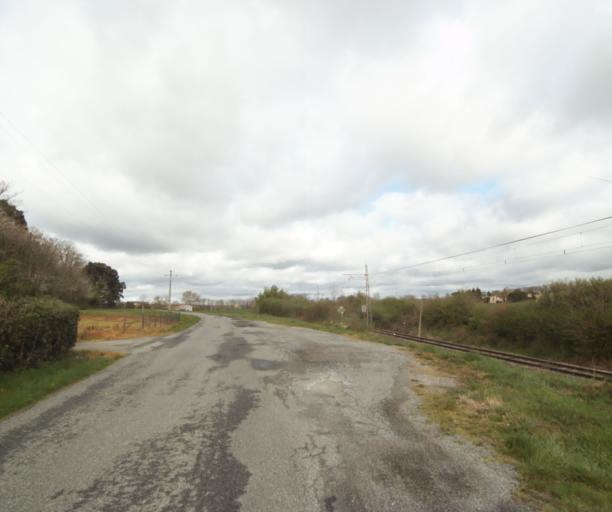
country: FR
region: Midi-Pyrenees
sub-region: Departement de l'Ariege
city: Saverdun
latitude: 43.2420
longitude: 1.5626
